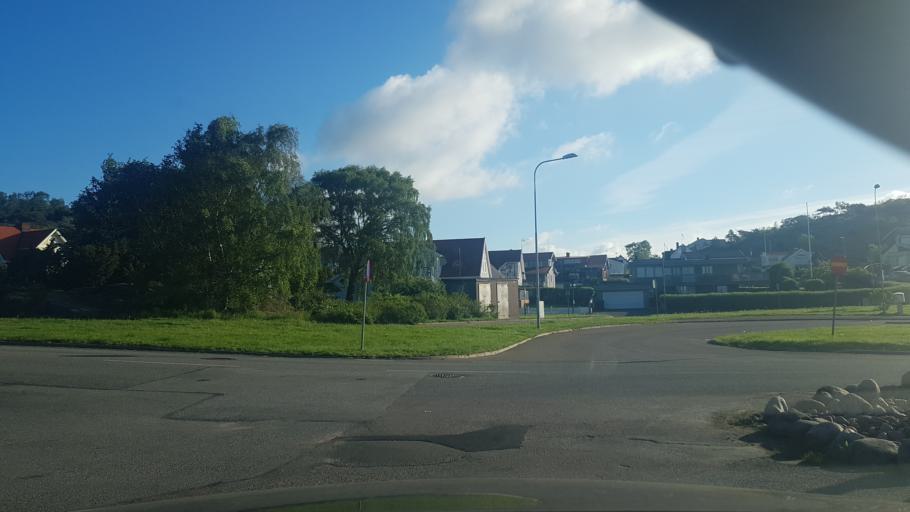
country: SE
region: Vaestra Goetaland
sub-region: Goteborg
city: Majorna
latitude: 57.6376
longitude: 11.8725
